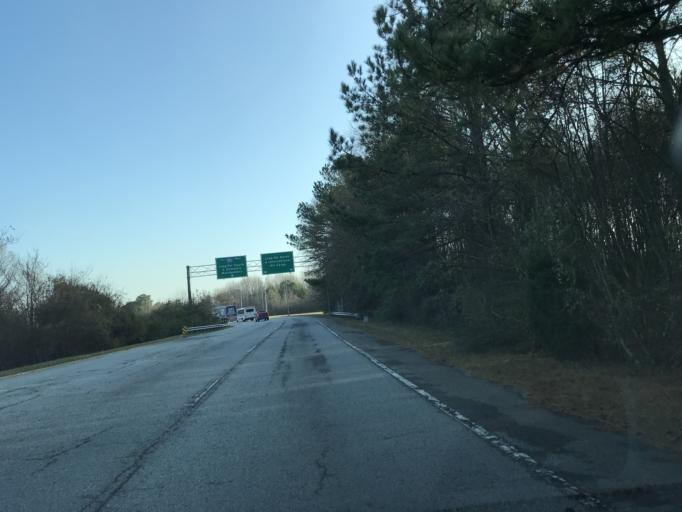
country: US
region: Georgia
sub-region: Fulton County
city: Hapeville
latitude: 33.6301
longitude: -84.4121
